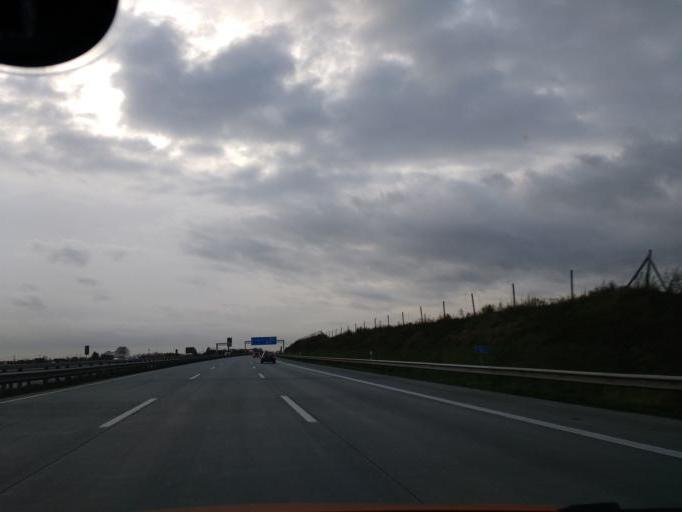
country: DE
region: Lower Saxony
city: Lengenbostel
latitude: 53.2964
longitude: 9.5275
